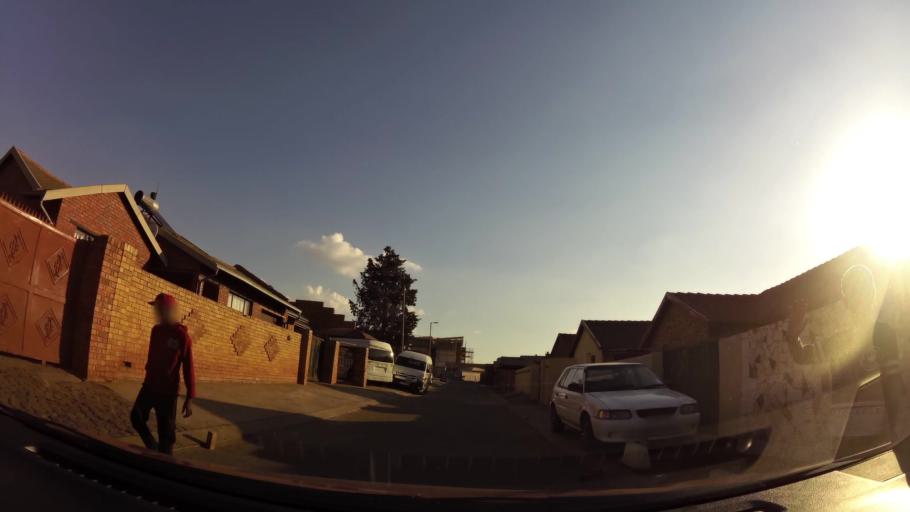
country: ZA
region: Gauteng
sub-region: City of Johannesburg Metropolitan Municipality
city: Soweto
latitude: -26.2269
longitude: 27.8568
